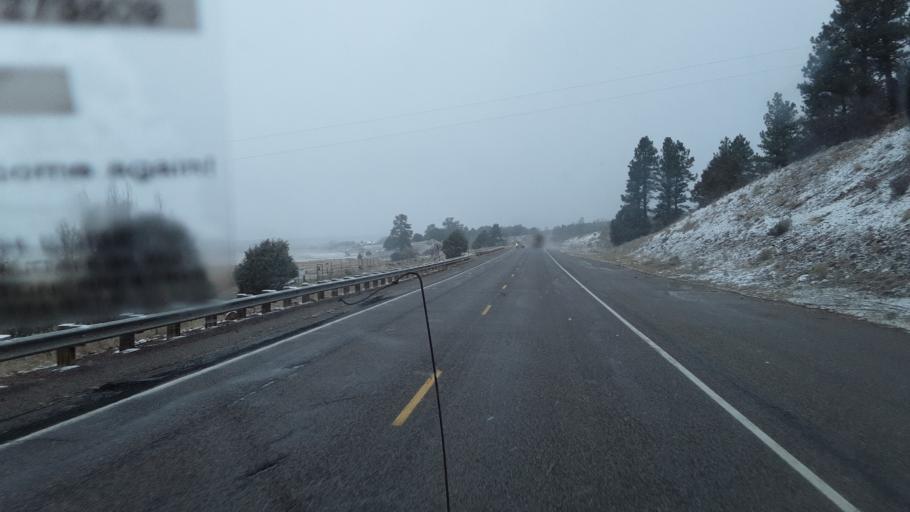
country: US
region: New Mexico
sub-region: Rio Arriba County
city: Tierra Amarilla
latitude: 36.7892
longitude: -106.5594
